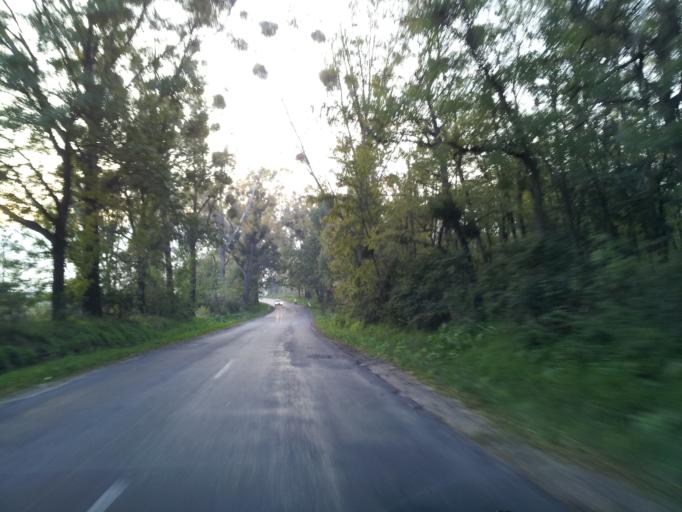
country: HU
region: Komarom-Esztergom
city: Kisber
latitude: 47.4720
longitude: 17.9429
